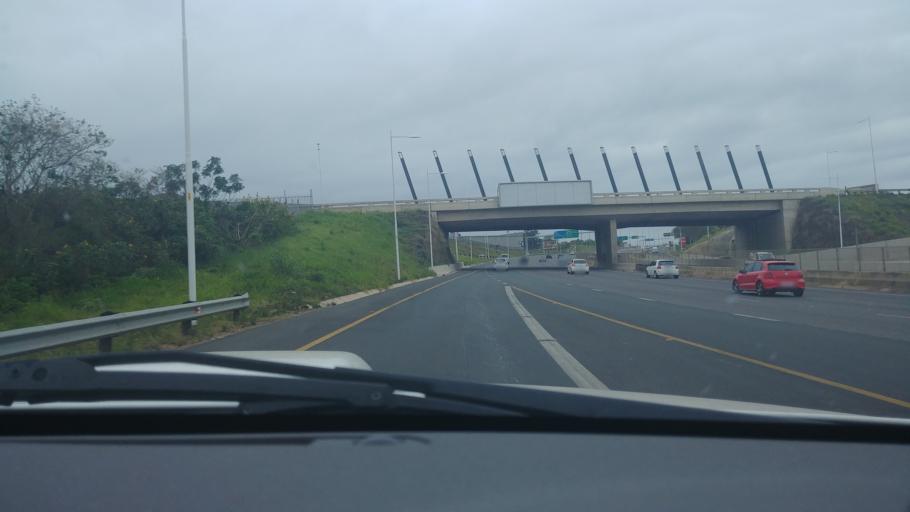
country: ZA
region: KwaZulu-Natal
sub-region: eThekwini Metropolitan Municipality
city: Durban
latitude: -29.7109
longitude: 31.0511
